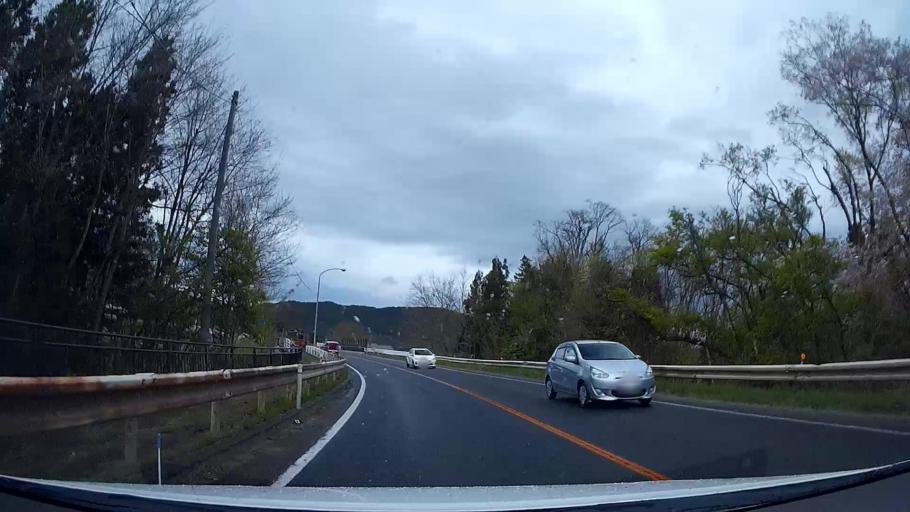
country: JP
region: Yamagata
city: Takahata
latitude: 38.0724
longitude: 140.1843
